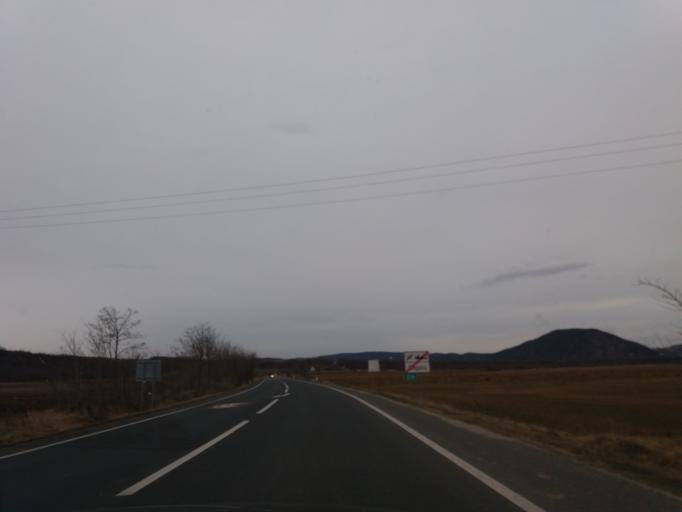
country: RO
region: Hunedoara
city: Bucium-Orlea
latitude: 45.5652
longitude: 22.9736
